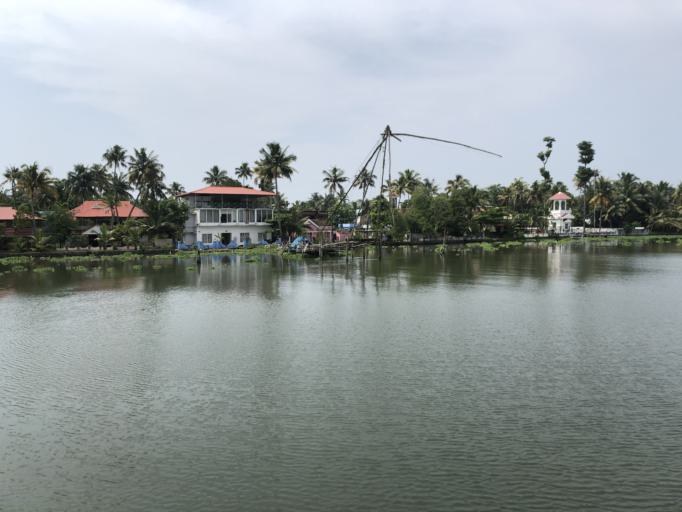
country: IN
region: Kerala
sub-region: Ernakulam
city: Cochin
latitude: 9.9946
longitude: 76.2664
